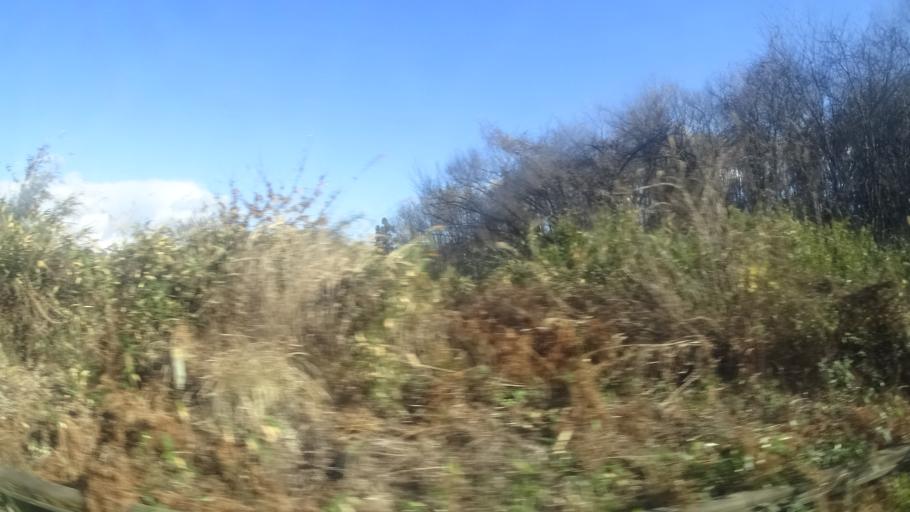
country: JP
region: Fukushima
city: Namie
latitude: 37.6785
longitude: 140.9715
